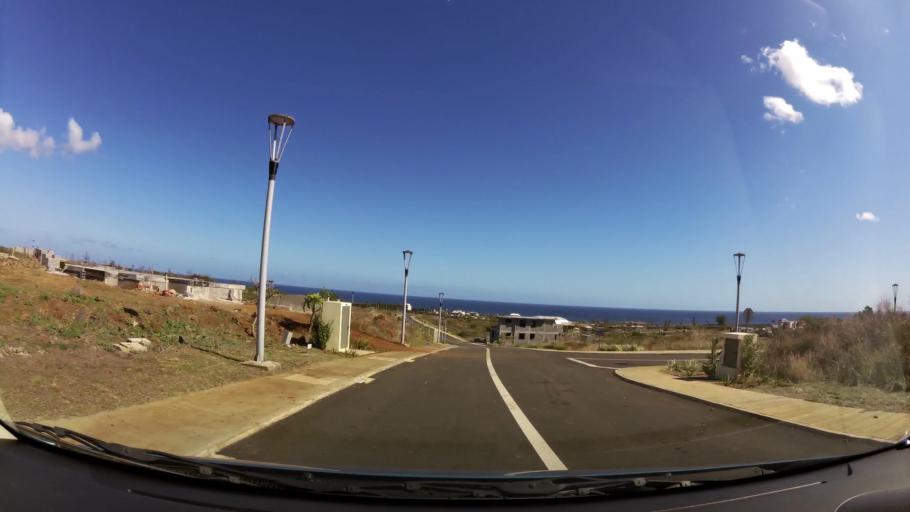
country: MU
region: Black River
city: Flic en Flac
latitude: -20.2703
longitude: 57.3848
